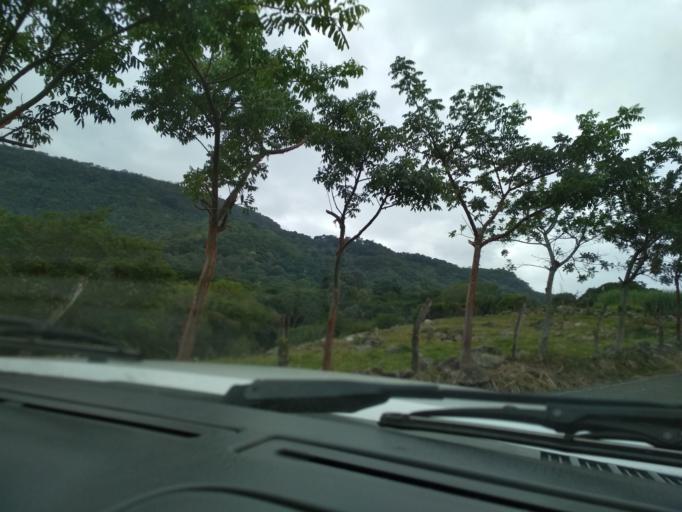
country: MX
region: Veracruz
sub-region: Actopan
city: Trapiche del Rosario
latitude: 19.5617
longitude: -96.7938
